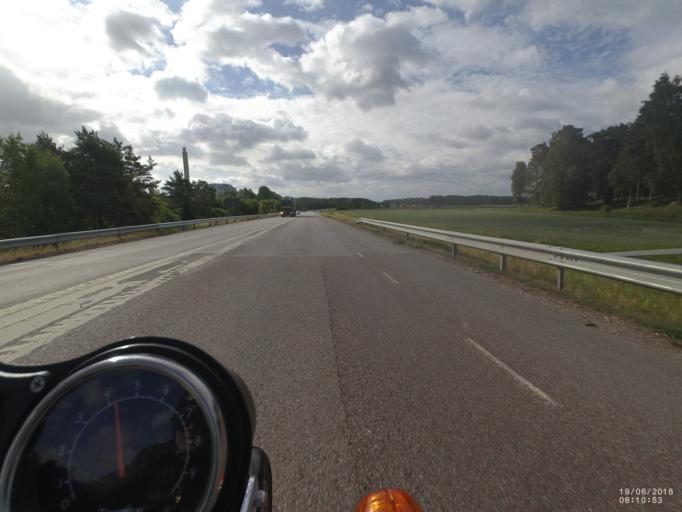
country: SE
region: Soedermanland
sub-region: Nykopings Kommun
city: Nykoping
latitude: 58.7453
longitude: 16.9940
